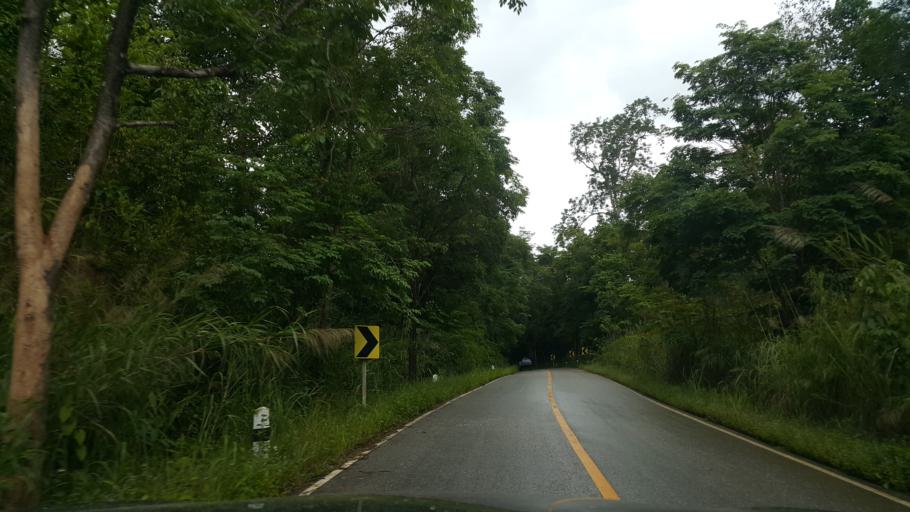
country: TH
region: Loei
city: Na Haeo
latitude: 17.4836
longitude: 100.8056
